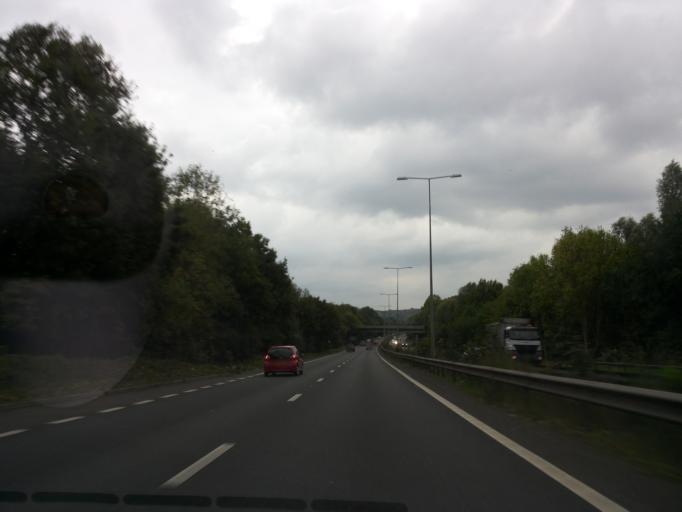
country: GB
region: England
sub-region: Kent
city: Dunkirk
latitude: 51.2987
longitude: 0.9381
